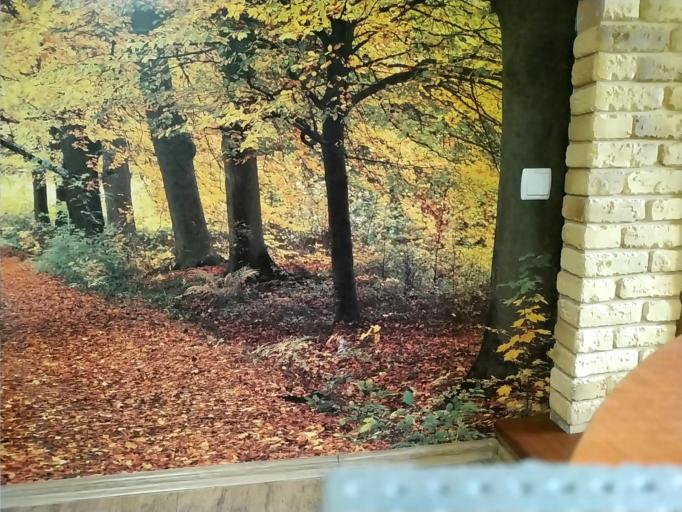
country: RU
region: Tverskaya
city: Kalashnikovo
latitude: 57.2579
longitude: 35.3495
